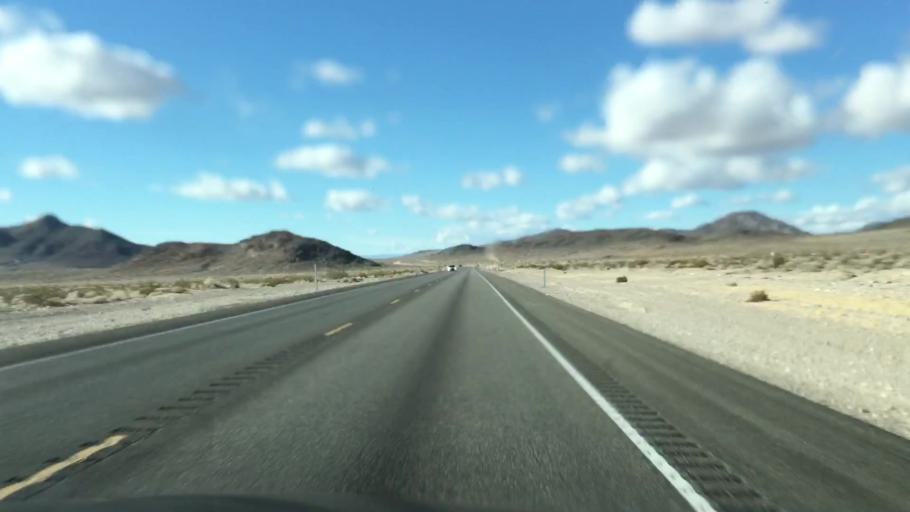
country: US
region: Nevada
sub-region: Nye County
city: Pahrump
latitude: 36.6200
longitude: -116.2918
